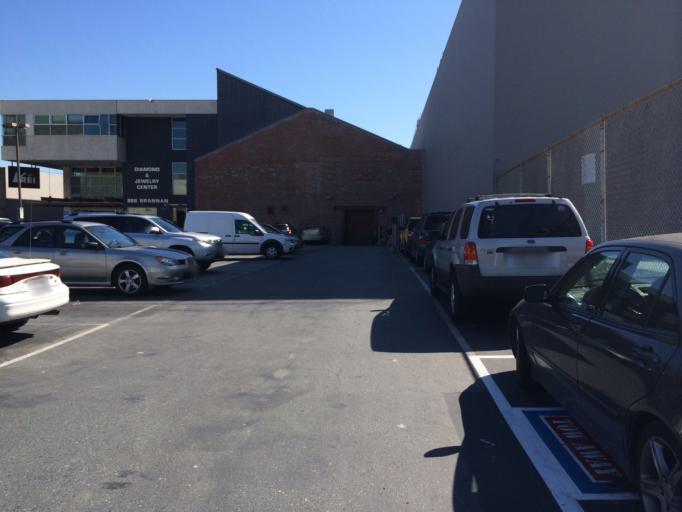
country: US
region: California
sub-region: San Francisco County
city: San Francisco
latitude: 37.7730
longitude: -122.4053
